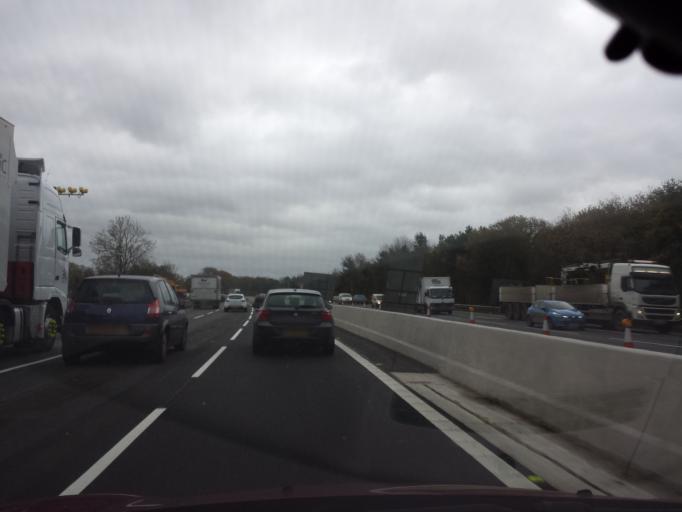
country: GB
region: England
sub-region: Surrey
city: Windlesham
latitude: 51.3587
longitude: -0.6616
